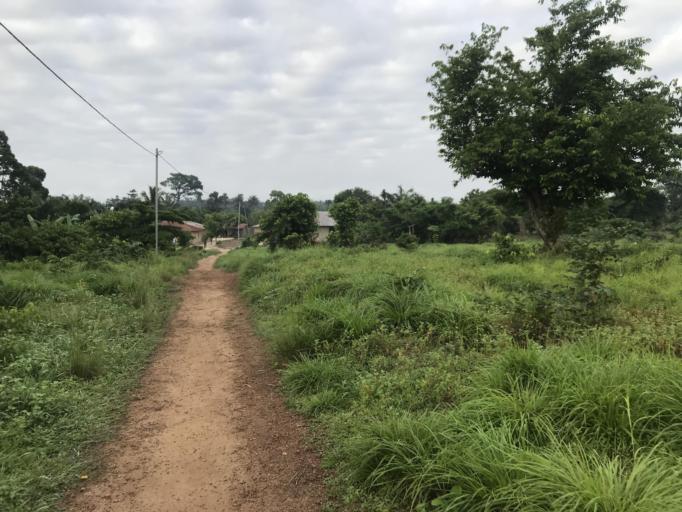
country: SL
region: Eastern Province
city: Pendembu
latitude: 8.0947
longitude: -10.6964
